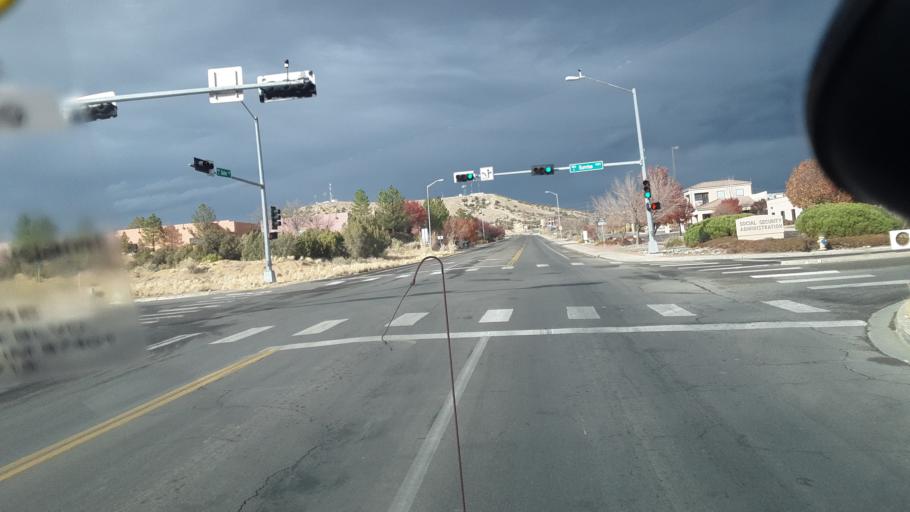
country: US
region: New Mexico
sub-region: San Juan County
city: Farmington
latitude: 36.7694
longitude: -108.1852
